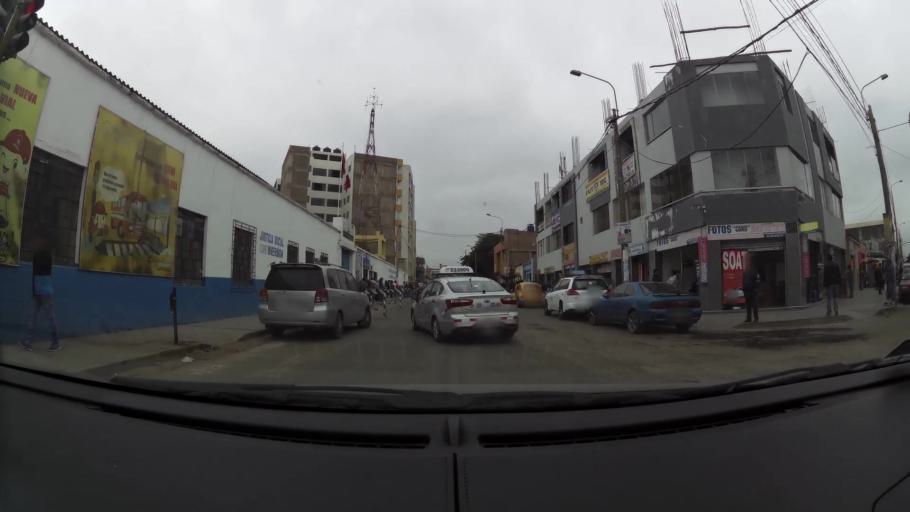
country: PE
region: La Libertad
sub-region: Provincia de Trujillo
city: Trujillo
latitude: -8.1179
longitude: -79.0249
